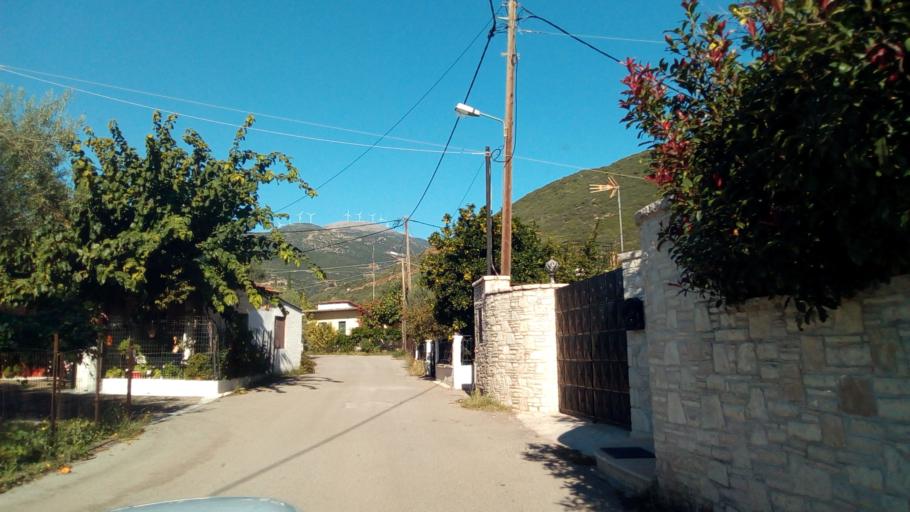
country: GR
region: West Greece
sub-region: Nomos Aitolias kai Akarnanias
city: Nafpaktos
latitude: 38.4091
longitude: 21.8539
